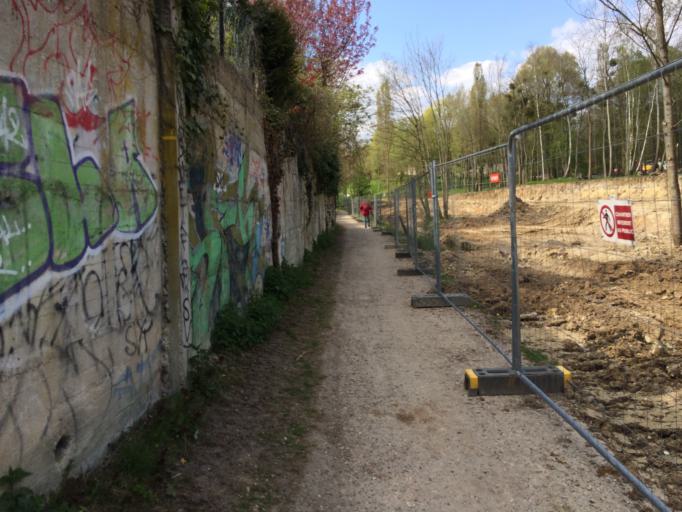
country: FR
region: Ile-de-France
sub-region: Departement de l'Essonne
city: Igny
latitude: 48.7478
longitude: 2.2263
